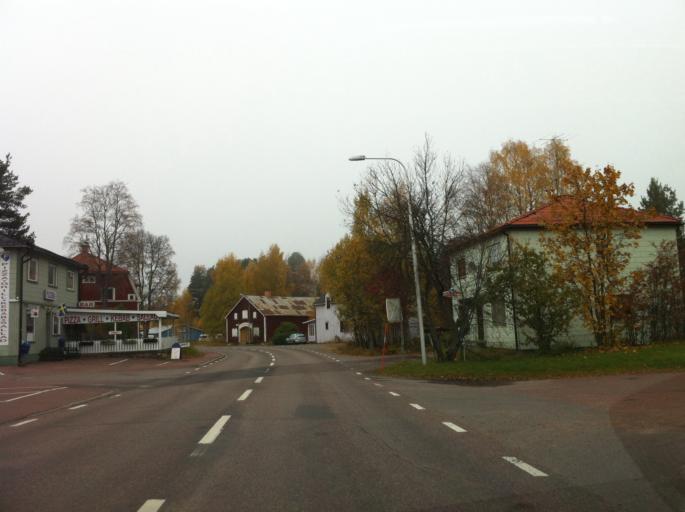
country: NO
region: Hedmark
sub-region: Trysil
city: Innbygda
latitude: 61.6940
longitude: 13.1368
